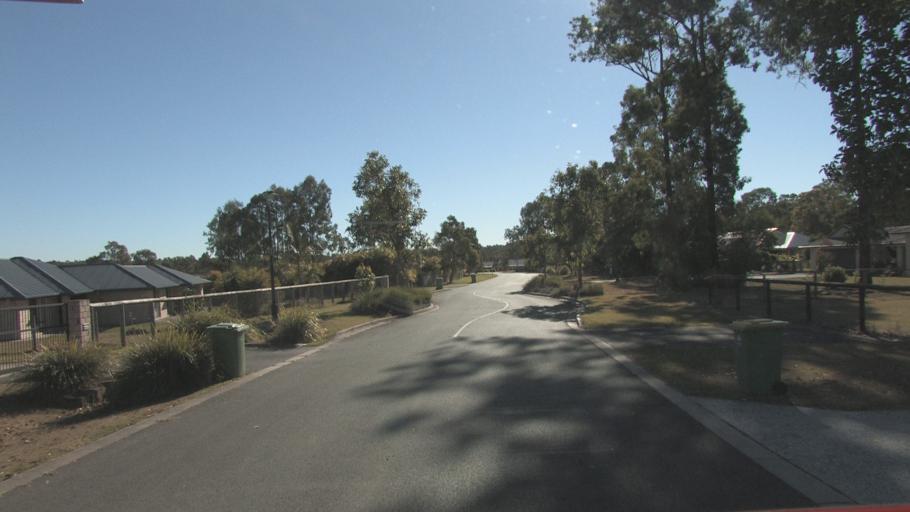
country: AU
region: Queensland
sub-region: Logan
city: North Maclean
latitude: -27.7578
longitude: 152.9665
